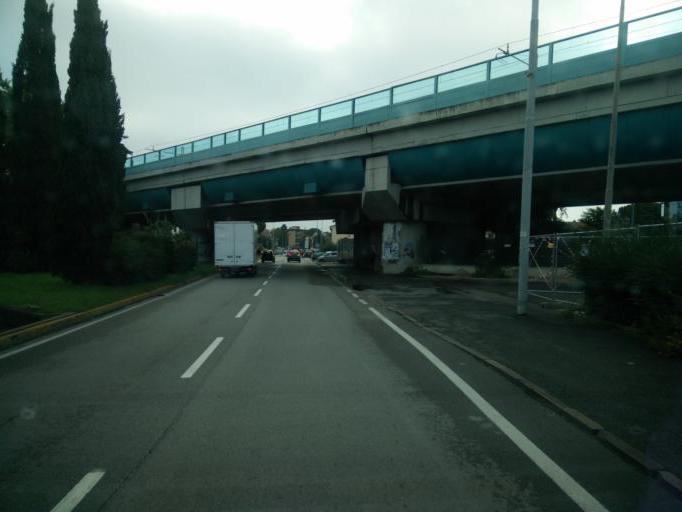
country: IT
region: Tuscany
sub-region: Province of Florence
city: Mantignano-Ugnano
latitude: 43.8005
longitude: 11.1916
